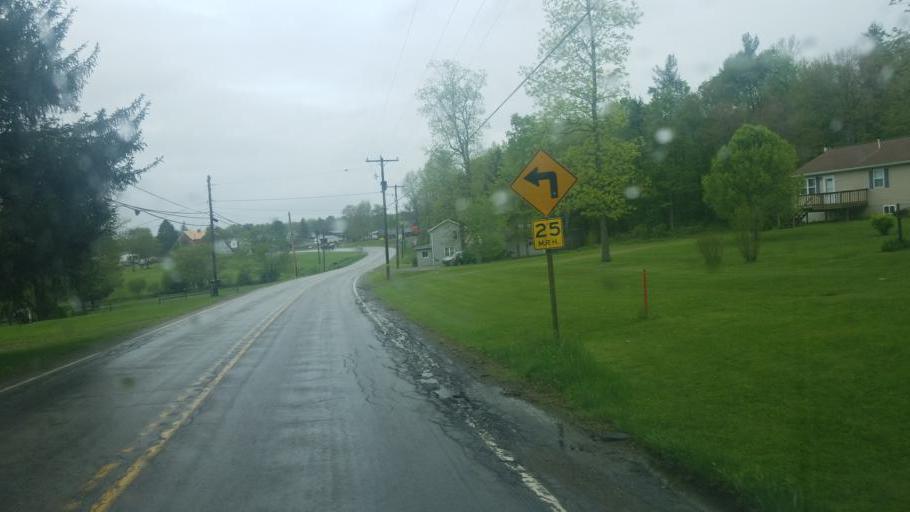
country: US
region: Pennsylvania
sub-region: Clarion County
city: Marianne
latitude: 41.3819
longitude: -79.3183
